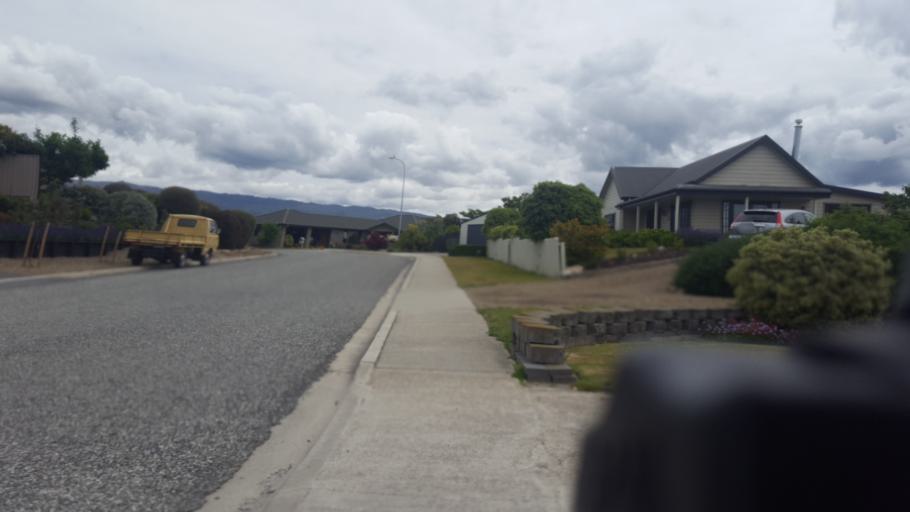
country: NZ
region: Otago
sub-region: Queenstown-Lakes District
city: Wanaka
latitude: -45.2523
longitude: 169.3828
